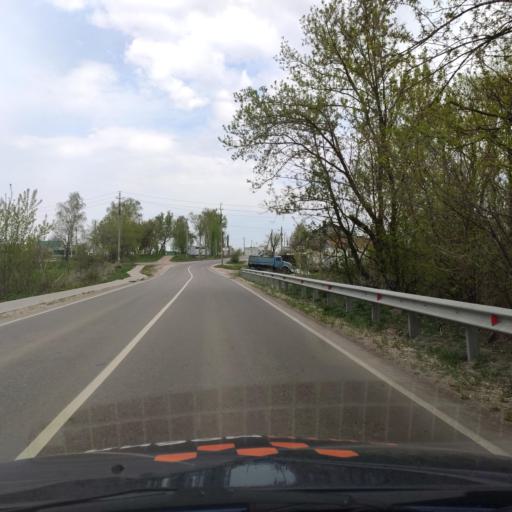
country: RU
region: Voronezj
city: Podgornoye
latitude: 51.8849
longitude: 39.1726
